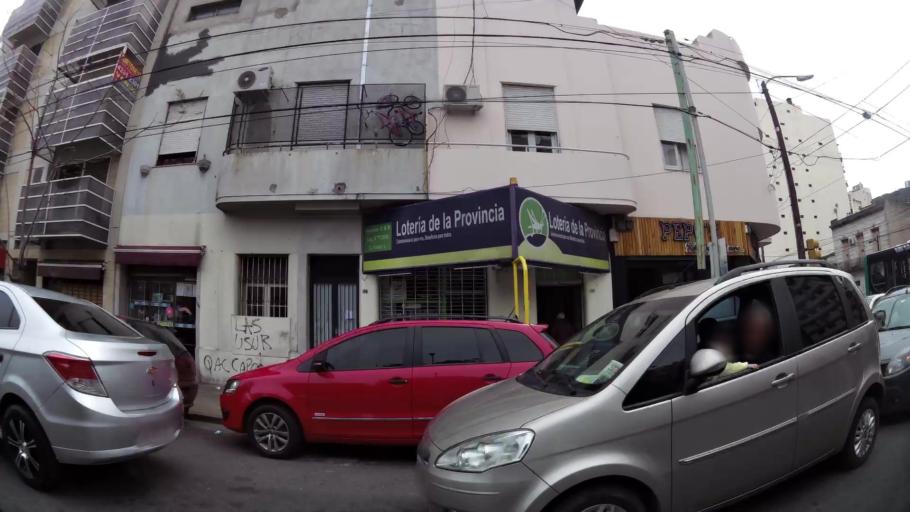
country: AR
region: Buenos Aires
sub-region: Partido de Avellaneda
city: Avellaneda
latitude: -34.6635
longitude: -58.3672
